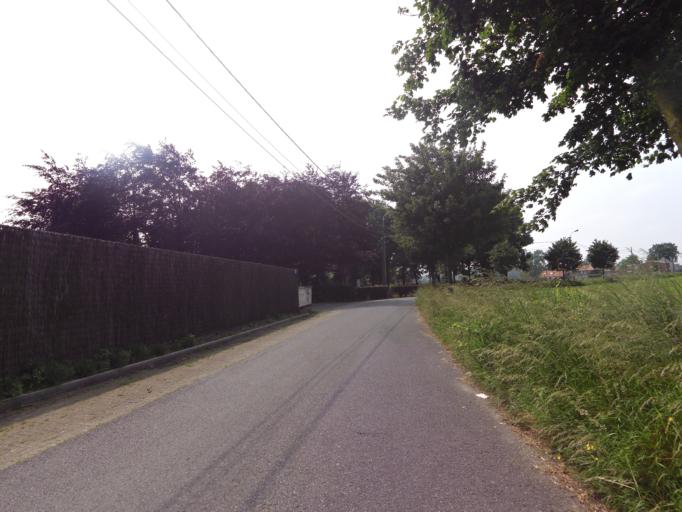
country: BE
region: Flanders
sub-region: Provincie West-Vlaanderen
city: Ichtegem
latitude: 51.1182
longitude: 3.0650
